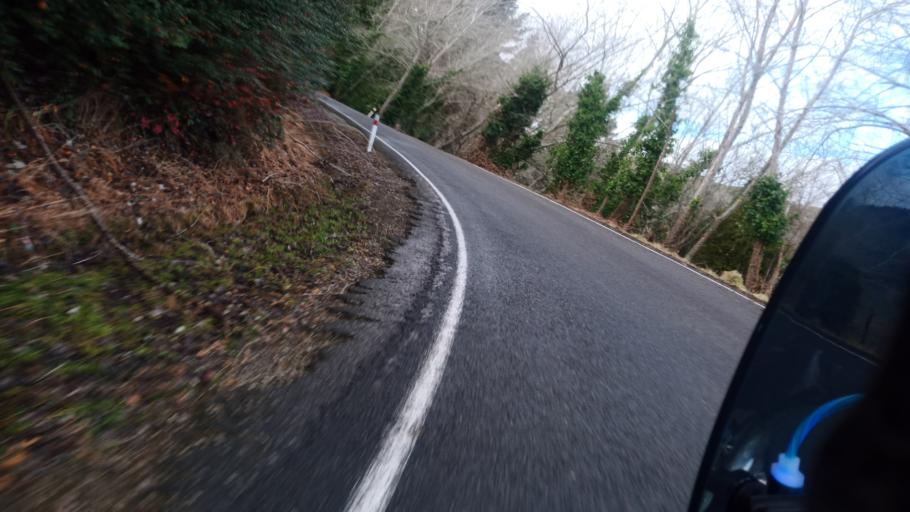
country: NZ
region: Gisborne
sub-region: Gisborne District
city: Gisborne
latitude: -38.4311
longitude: 177.9114
